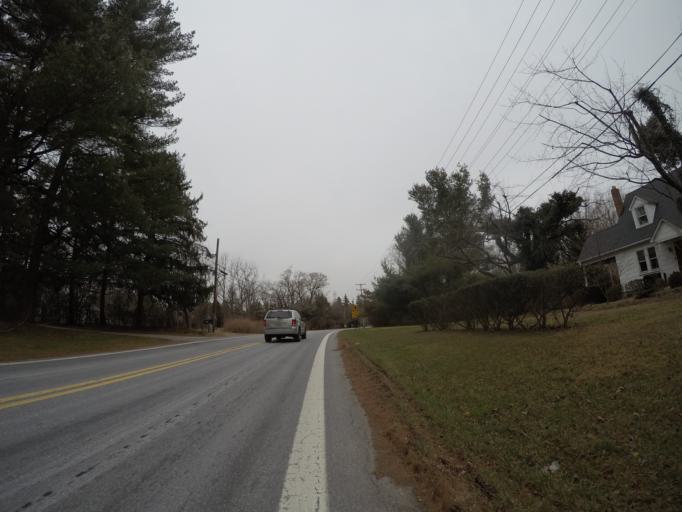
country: US
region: Maryland
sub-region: Howard County
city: Ilchester
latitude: 39.2211
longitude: -76.7891
